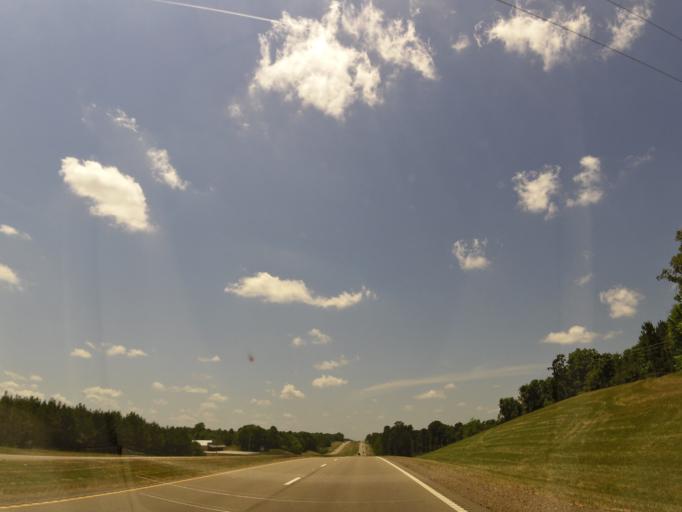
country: US
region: Mississippi
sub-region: Pontotoc County
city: Pontotoc
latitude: 34.2895
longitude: -89.1834
